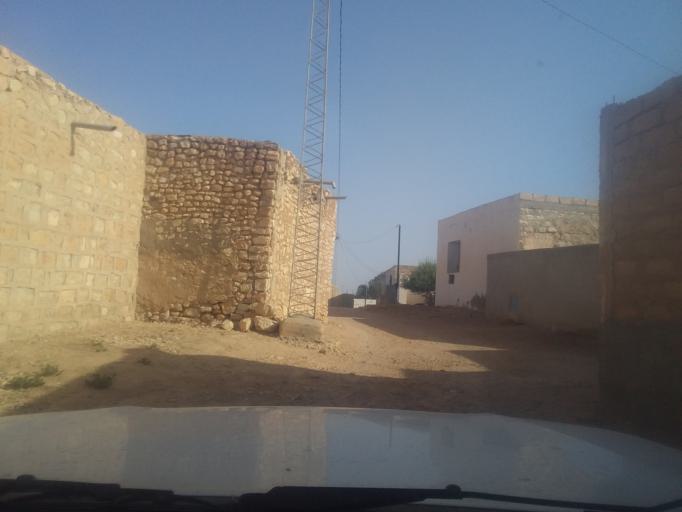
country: TN
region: Qabis
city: Matmata
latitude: 33.5846
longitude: 10.2696
